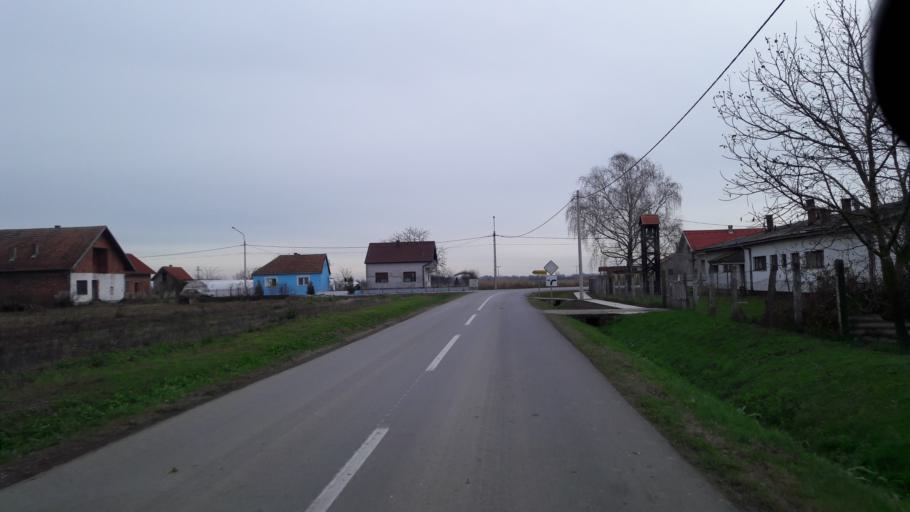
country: HR
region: Osjecko-Baranjska
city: Vladislavci
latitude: 45.4393
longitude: 18.5981
